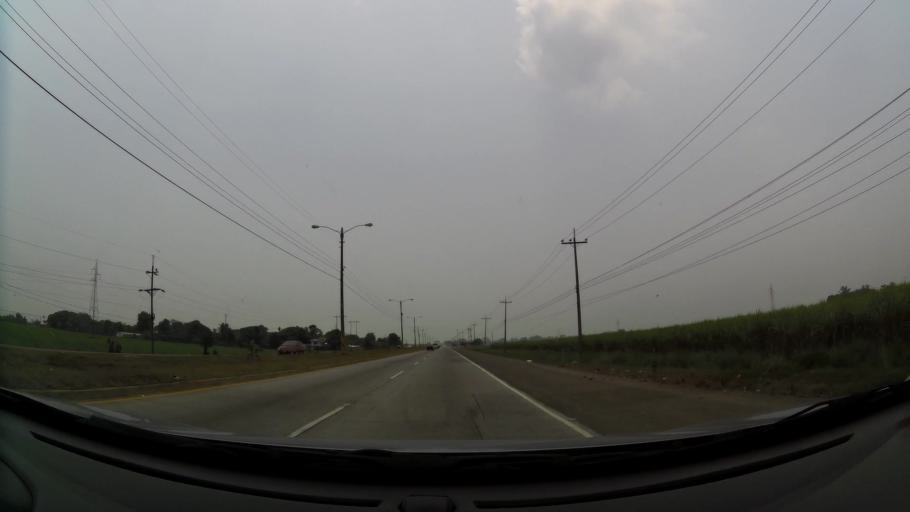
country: HN
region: Cortes
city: La Lima
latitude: 15.4117
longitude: -87.8657
